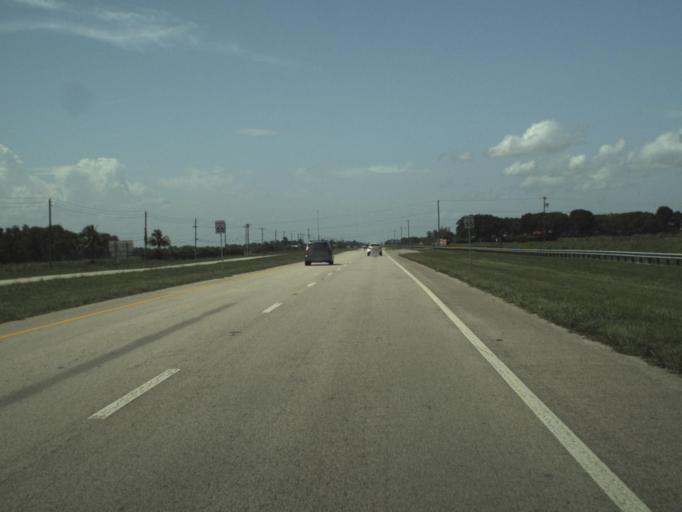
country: US
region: Florida
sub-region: Palm Beach County
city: Villages of Oriole
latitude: 26.4989
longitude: -80.2050
